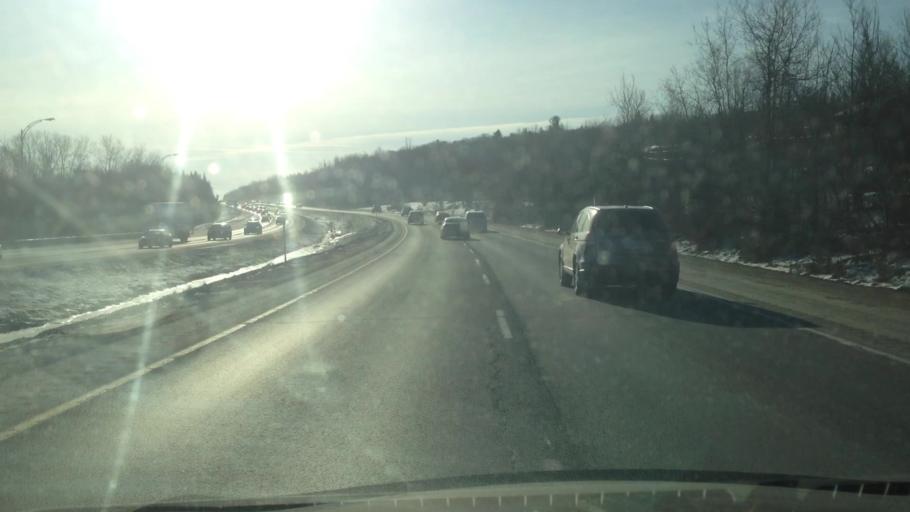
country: CA
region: Quebec
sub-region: Laurentides
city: Prevost
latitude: 45.8674
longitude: -74.0861
